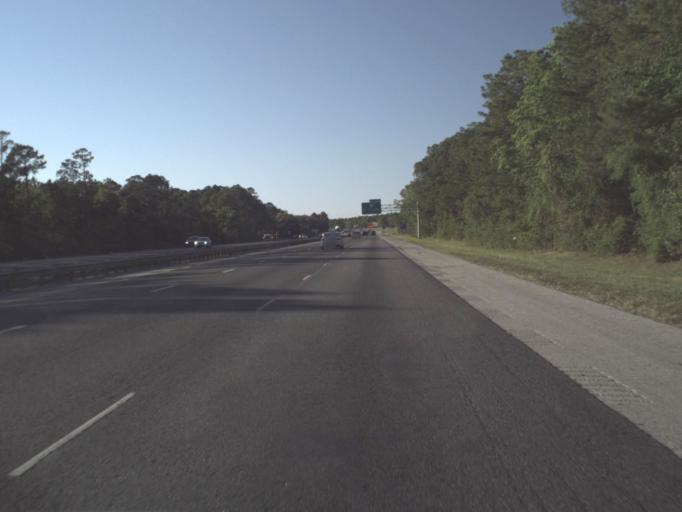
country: US
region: Florida
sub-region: Flagler County
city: Palm Coast
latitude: 29.6465
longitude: -81.2734
